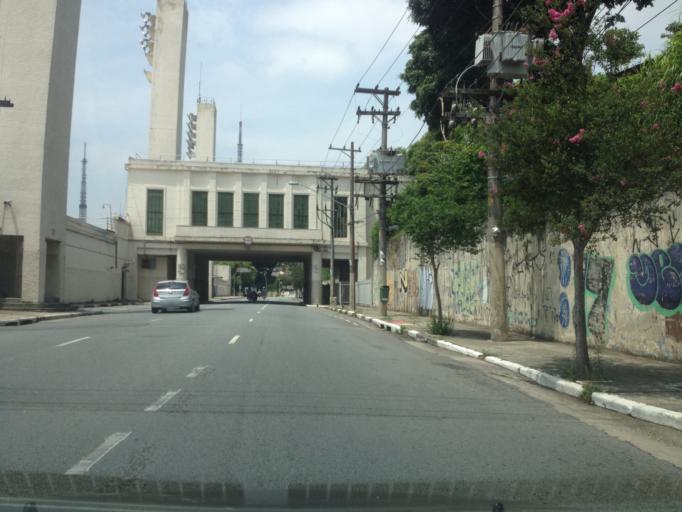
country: BR
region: Sao Paulo
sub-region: Sao Paulo
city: Sao Paulo
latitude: -23.5480
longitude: -46.6662
